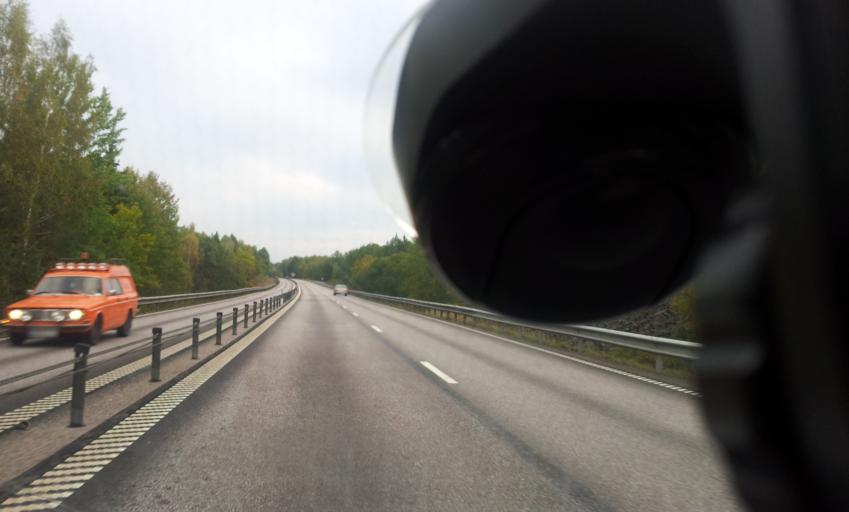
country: SE
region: Kalmar
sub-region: Oskarshamns Kommun
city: Oskarshamn
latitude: 57.2978
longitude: 16.4604
